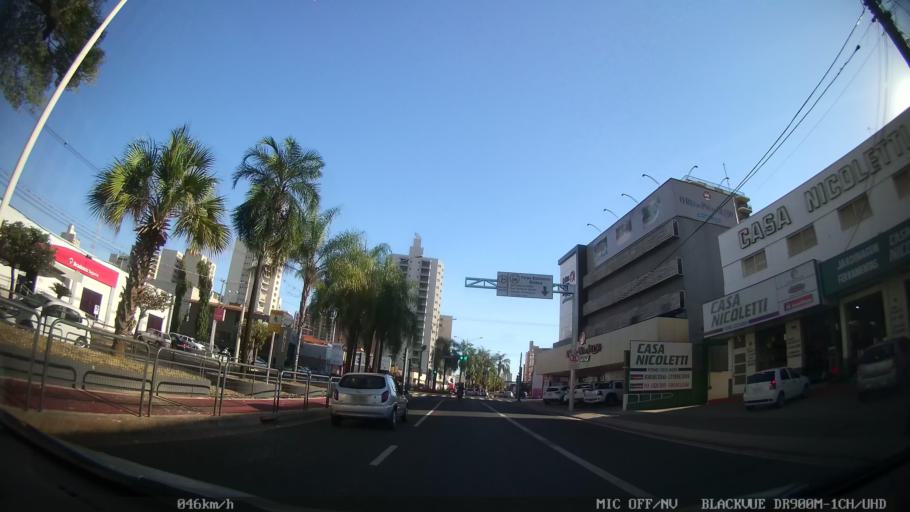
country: BR
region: Sao Paulo
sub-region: Sao Jose Do Rio Preto
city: Sao Jose do Rio Preto
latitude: -20.8098
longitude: -49.3839
